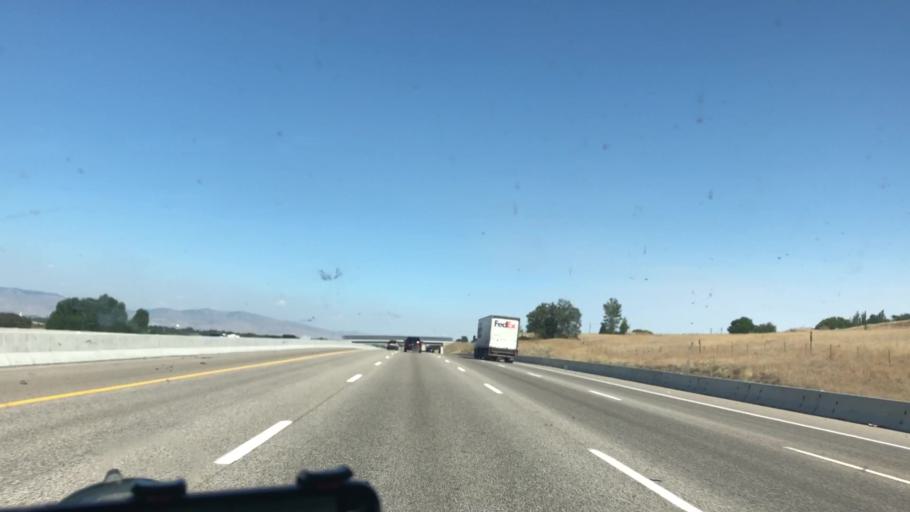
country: US
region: Idaho
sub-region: Ada County
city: Meridian
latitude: 43.5955
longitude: -116.4606
